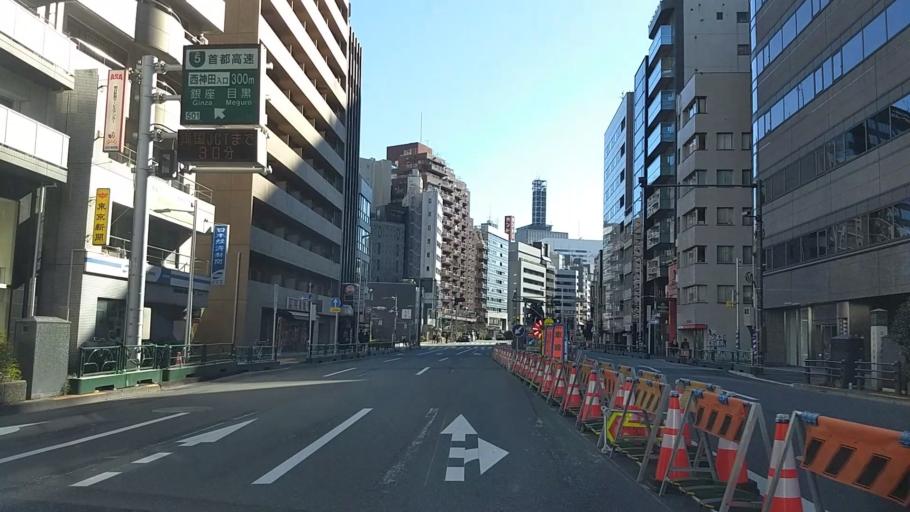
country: JP
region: Tokyo
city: Tokyo
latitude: 35.6991
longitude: 139.7492
